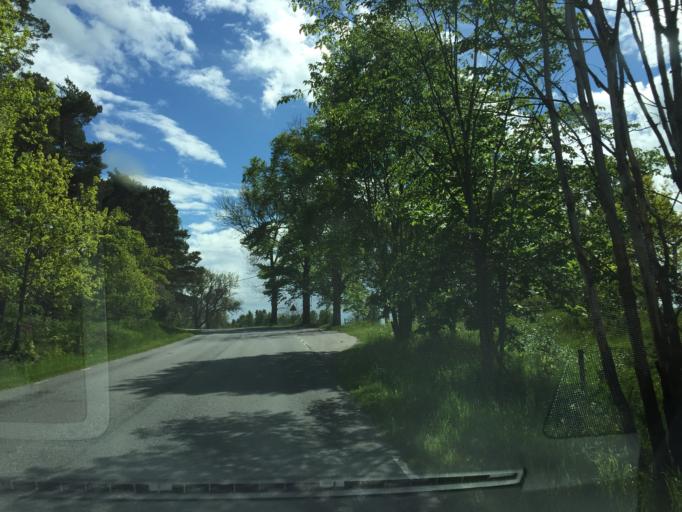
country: SE
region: OEstergoetland
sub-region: Norrkopings Kommun
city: Kimstad
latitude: 58.5212
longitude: 15.9720
